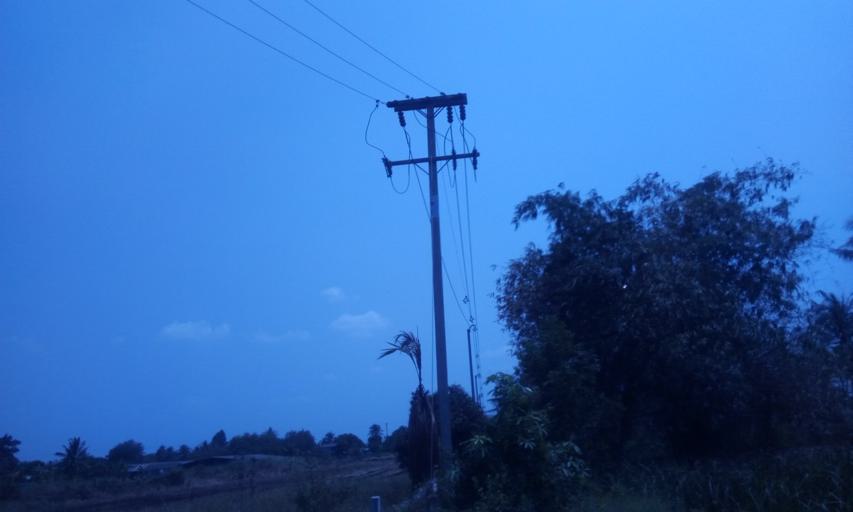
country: TH
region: Chachoengsao
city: Bang Nam Priao
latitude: 13.8677
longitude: 100.9668
